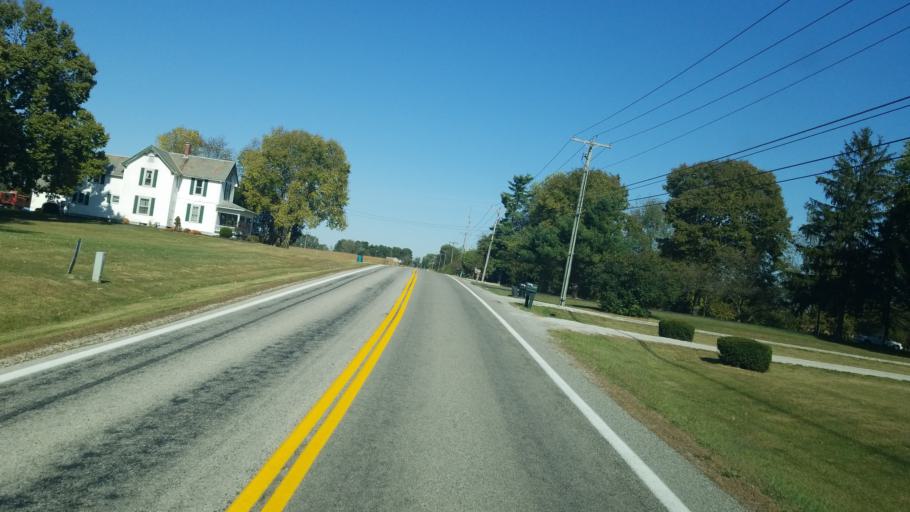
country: US
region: Ohio
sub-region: Marion County
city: Prospect
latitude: 40.4659
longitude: -83.0792
